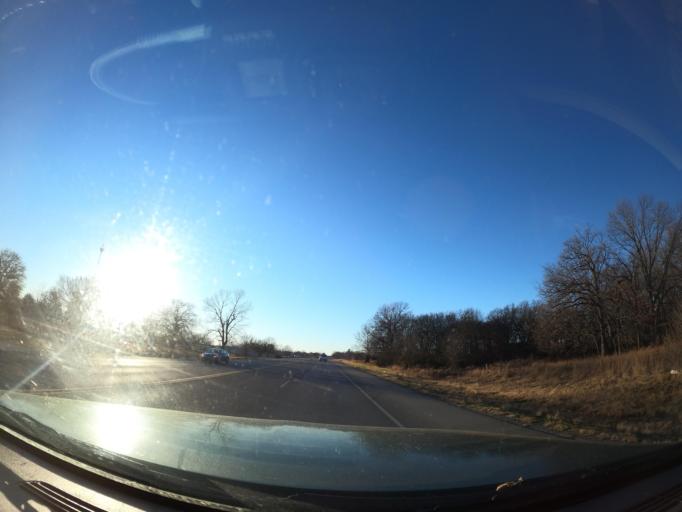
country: US
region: Oklahoma
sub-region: Pittsburg County
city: Krebs
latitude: 34.8940
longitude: -95.6335
